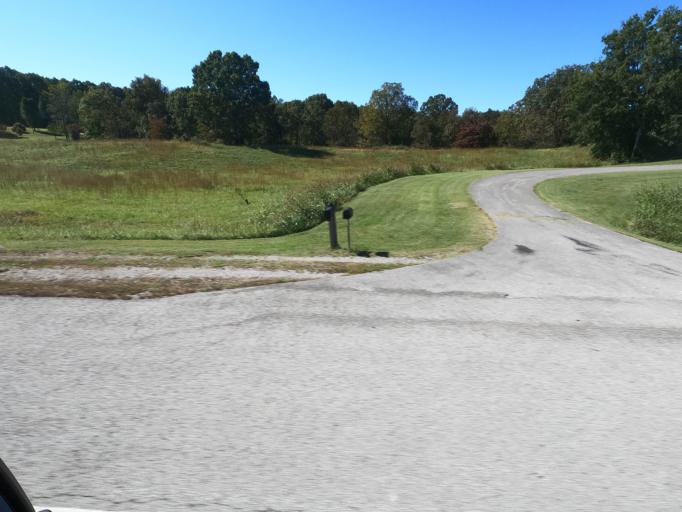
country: US
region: Tennessee
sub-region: Maury County
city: Mount Pleasant
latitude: 35.4544
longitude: -87.2675
